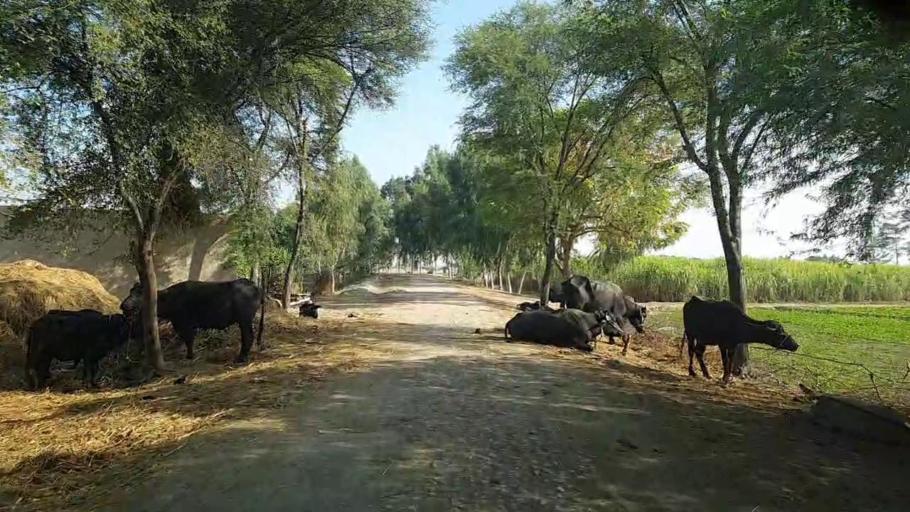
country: PK
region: Sindh
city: Darya Khan Marri
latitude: 26.6534
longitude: 68.3583
